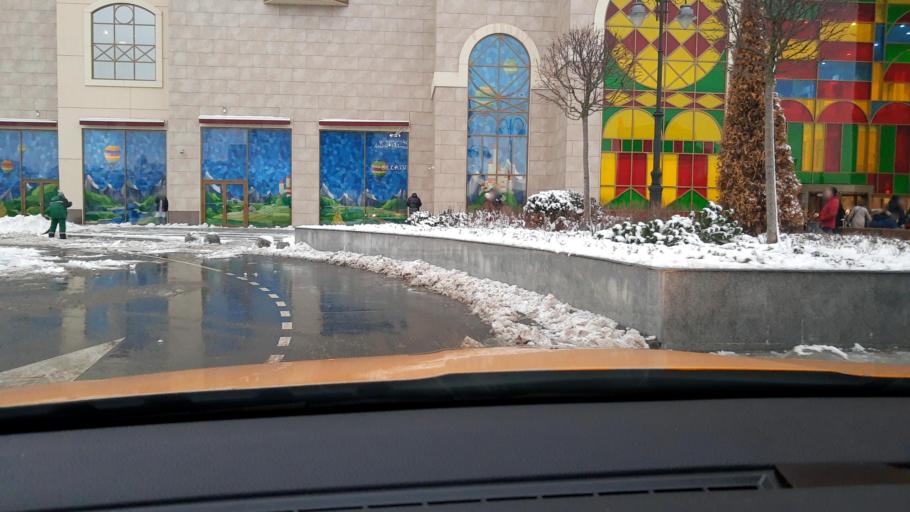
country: RU
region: Moskovskaya
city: Kozhukhovo
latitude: 55.6939
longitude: 37.6714
